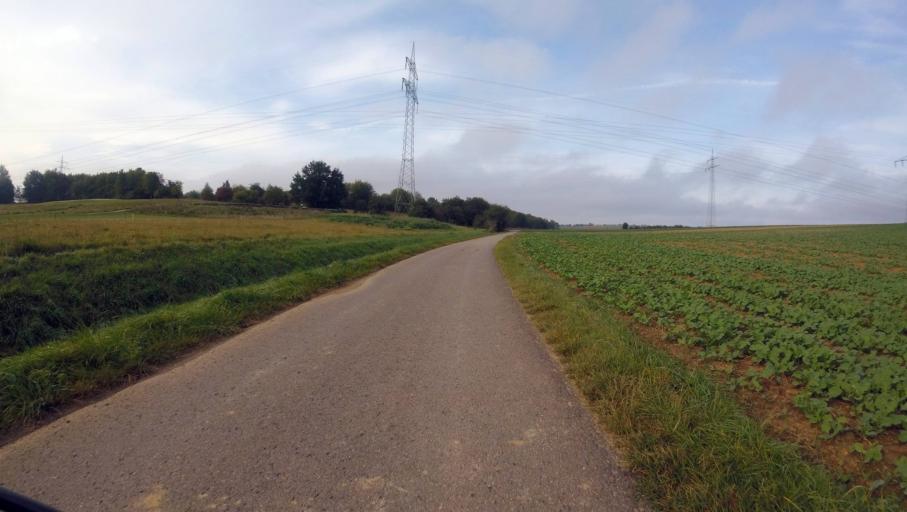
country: DE
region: Baden-Wuerttemberg
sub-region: Regierungsbezirk Stuttgart
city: Bondorf
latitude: 48.5336
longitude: 8.8076
